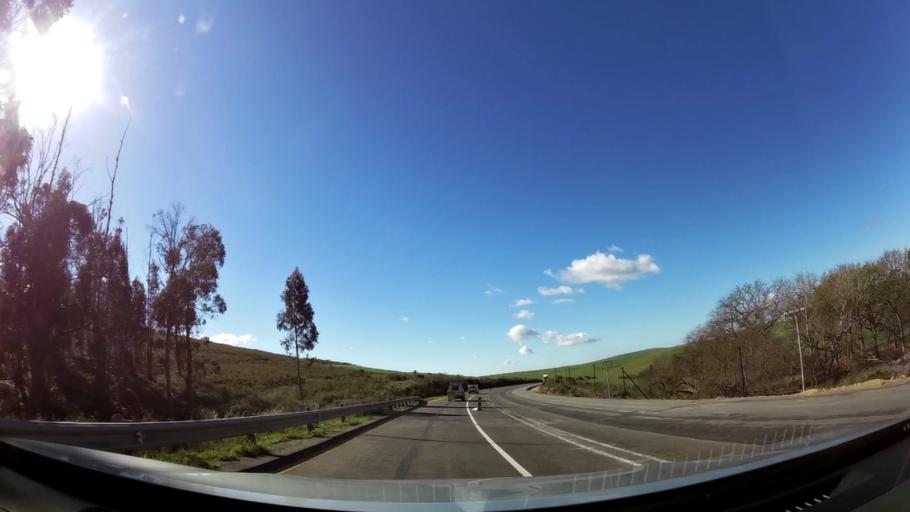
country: ZA
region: Western Cape
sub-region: Overberg District Municipality
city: Caledon
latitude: -34.2039
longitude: 19.5930
